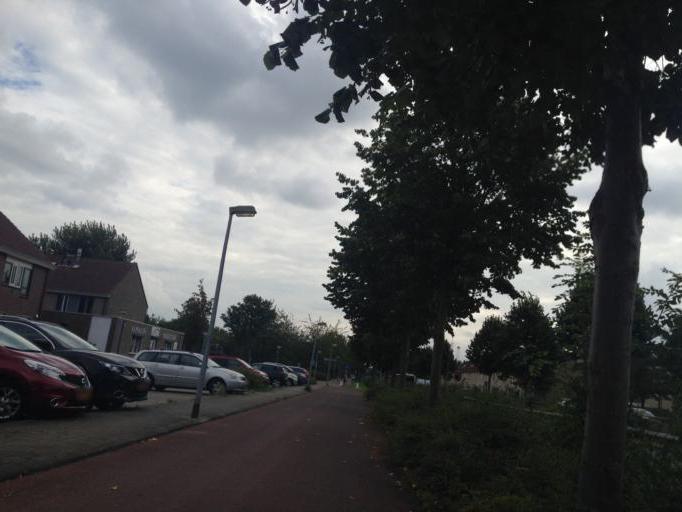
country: NL
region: Flevoland
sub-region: Gemeente Almere
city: Almere Stad
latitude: 52.4006
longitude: 5.2694
